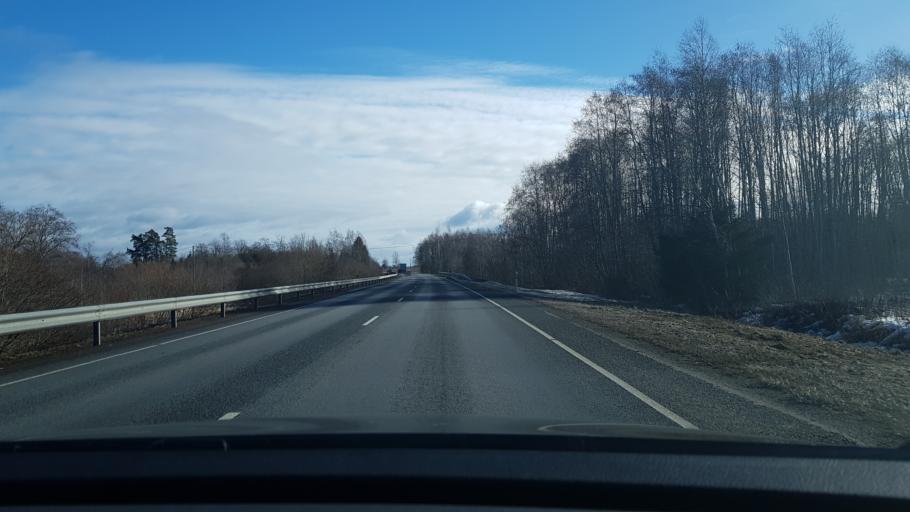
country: EE
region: Paernumaa
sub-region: Saarde vald
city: Kilingi-Nomme
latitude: 58.1940
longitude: 24.7534
